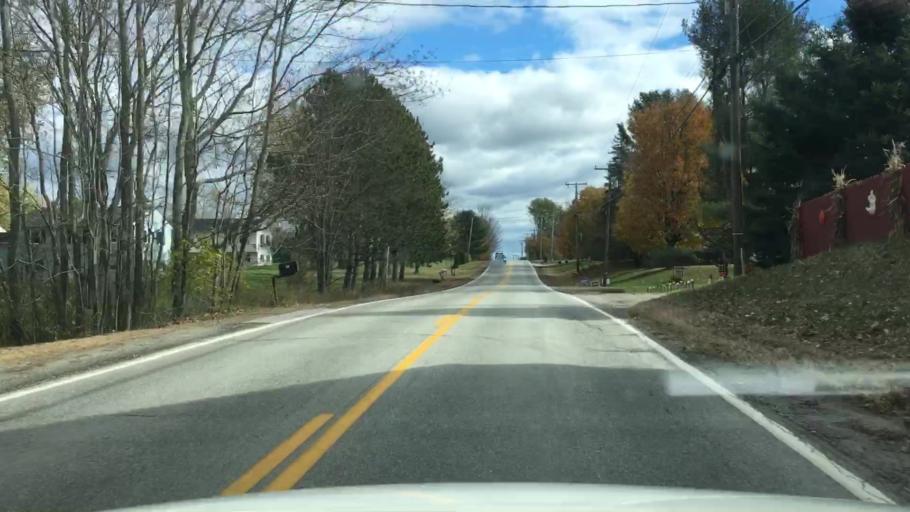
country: US
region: Maine
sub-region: Sagadahoc County
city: Richmond
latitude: 44.0934
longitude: -69.8351
